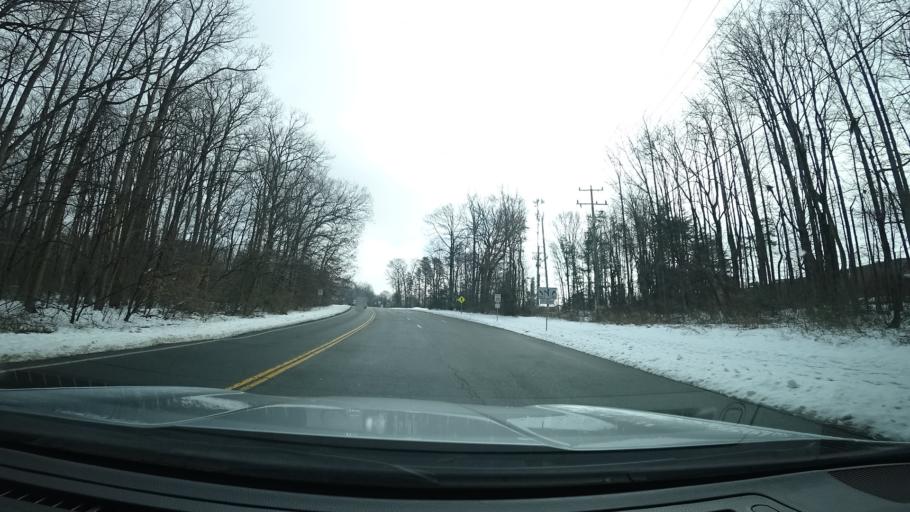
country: US
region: Virginia
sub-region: Fairfax County
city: Oak Hill
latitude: 38.9281
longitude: -77.3745
